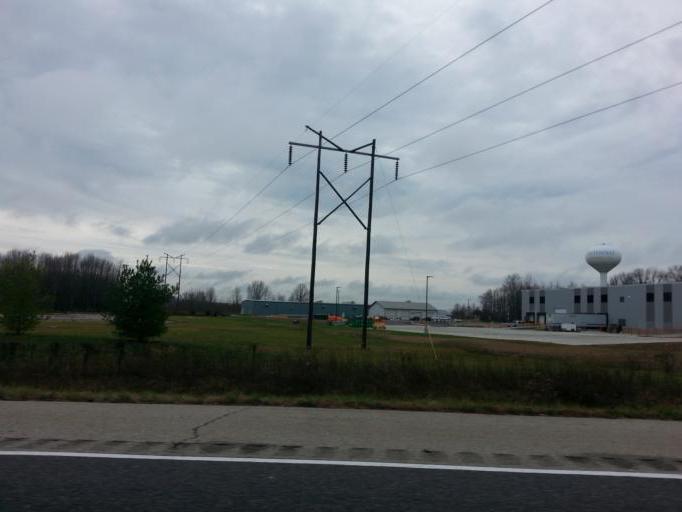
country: US
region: Indiana
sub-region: Ripley County
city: Batesville
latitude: 39.2996
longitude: -85.1912
